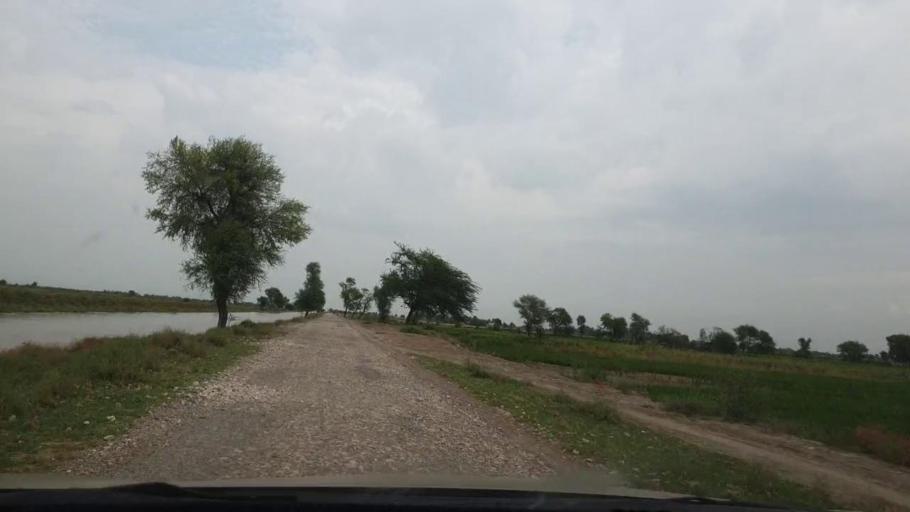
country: PK
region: Sindh
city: Ratodero
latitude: 27.8245
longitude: 68.3073
